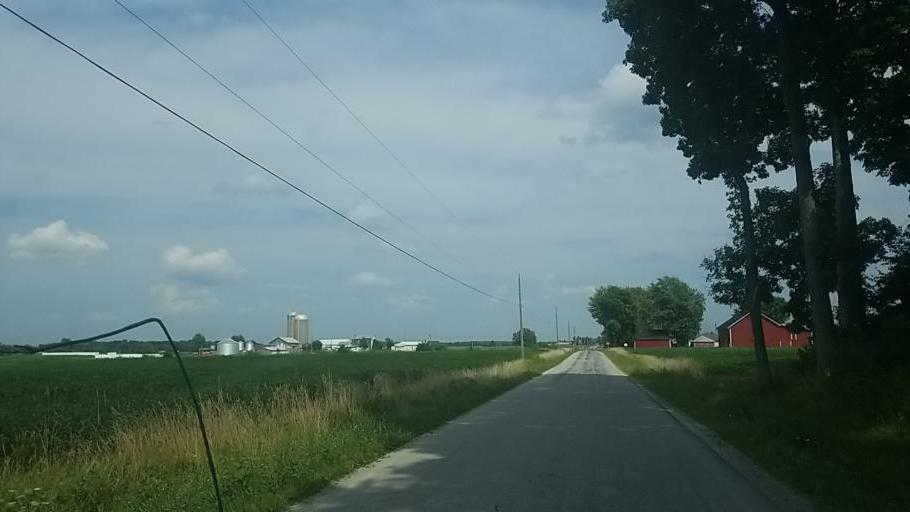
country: US
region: Ohio
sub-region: Hardin County
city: Forest
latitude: 40.8177
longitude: -83.4255
